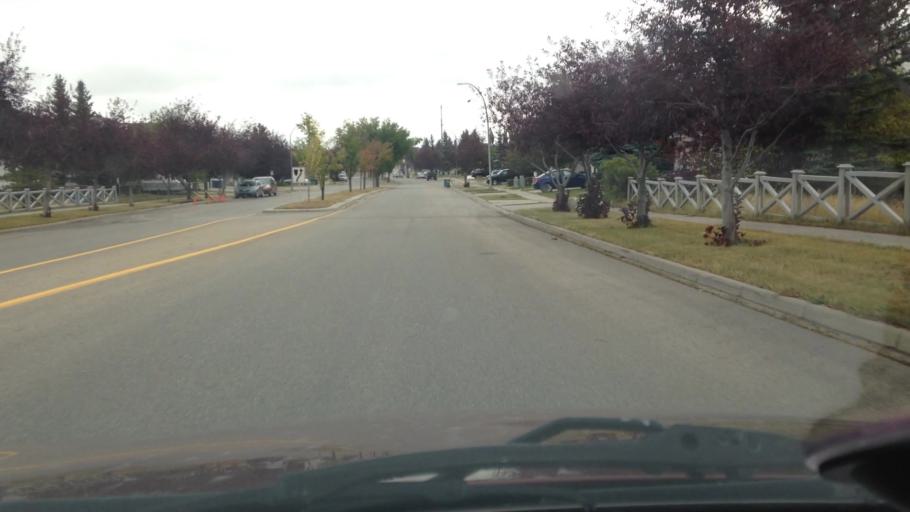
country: CA
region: Alberta
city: Calgary
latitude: 51.1469
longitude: -114.1147
